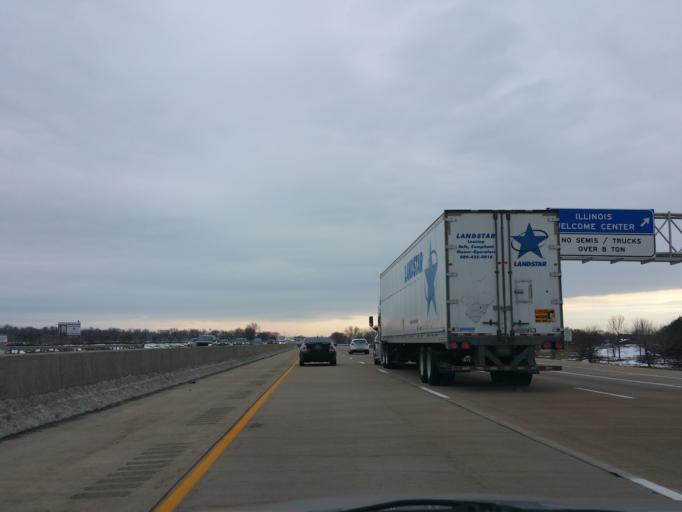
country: US
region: Illinois
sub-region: Winnebago County
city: South Beloit
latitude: 42.4838
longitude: -88.9951
